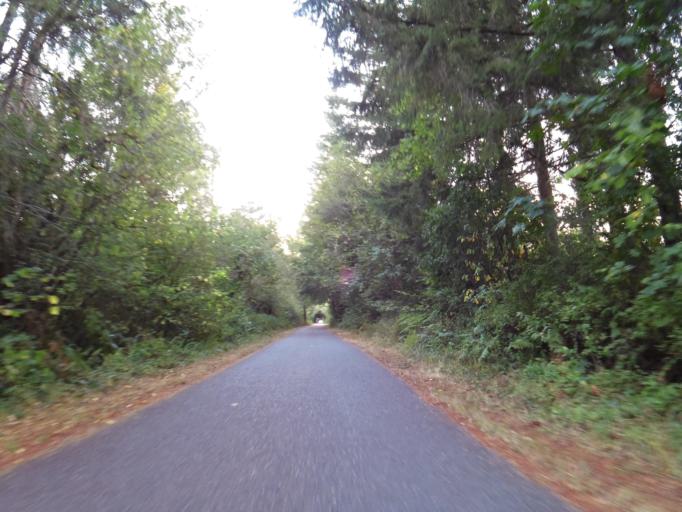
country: US
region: Washington
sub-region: Thurston County
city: Tenino
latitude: 46.8563
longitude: -122.8426
